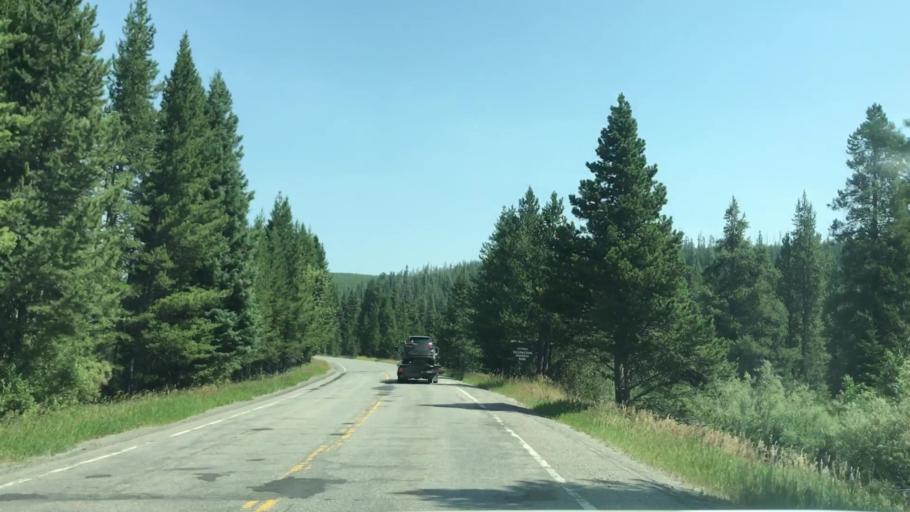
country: US
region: Montana
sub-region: Gallatin County
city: West Yellowstone
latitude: 44.8078
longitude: -111.0976
